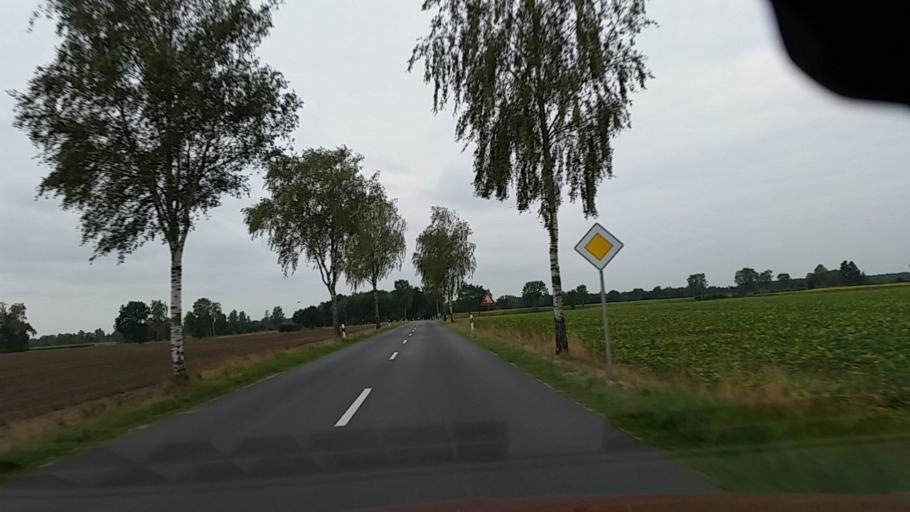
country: DE
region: Lower Saxony
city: Wittingen
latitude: 52.6654
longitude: 10.7017
